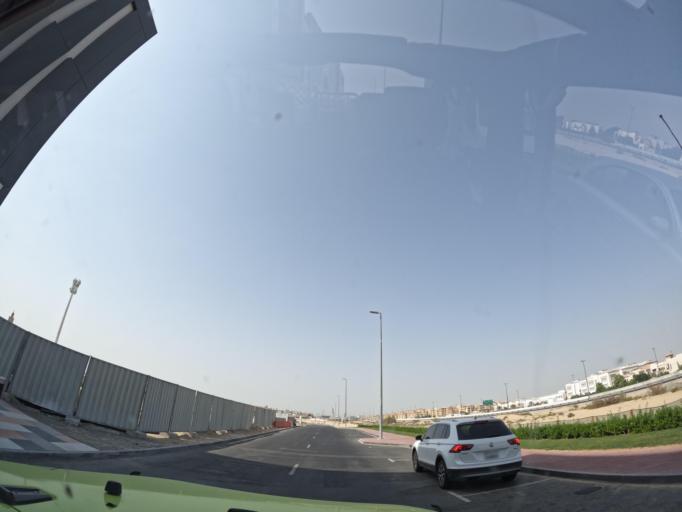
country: AE
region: Ash Shariqah
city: Sharjah
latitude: 25.2071
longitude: 55.4250
